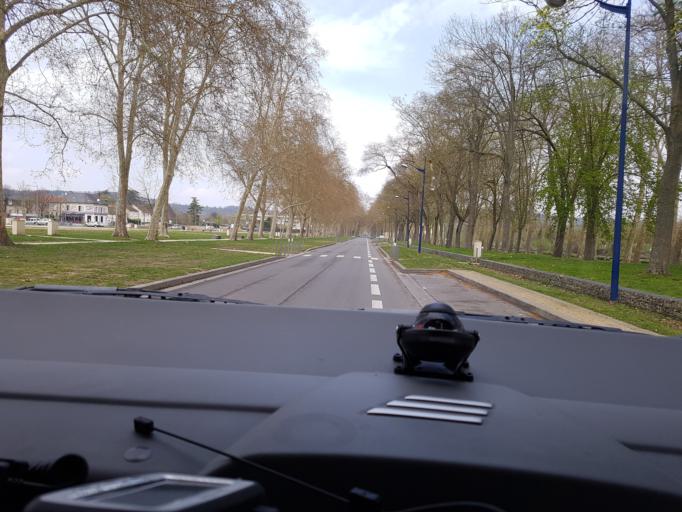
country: FR
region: Picardie
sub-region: Departement de l'Aisne
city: Soissons
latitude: 49.3848
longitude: 3.3294
